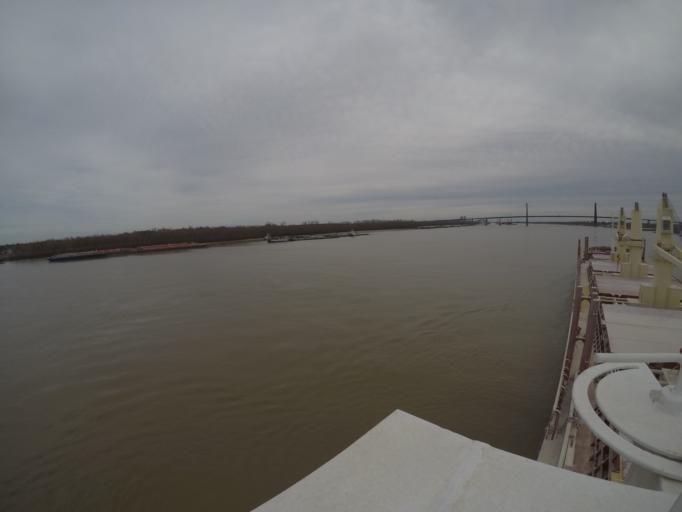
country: US
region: Louisiana
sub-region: Saint Charles Parish
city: New Sarpy
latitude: 29.9494
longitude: -90.3903
